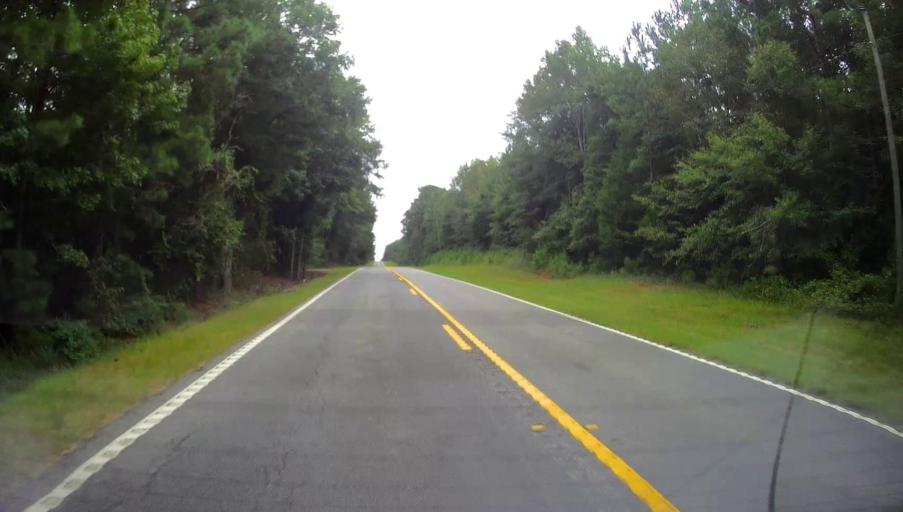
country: US
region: Georgia
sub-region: Dooly County
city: Unadilla
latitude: 32.2912
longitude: -83.8634
